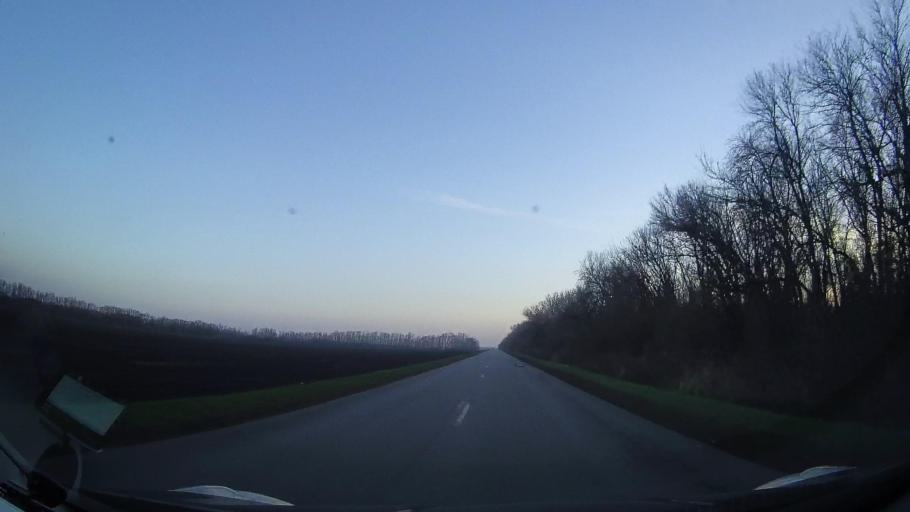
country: RU
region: Rostov
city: Zernograd
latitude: 46.9945
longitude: 40.3915
